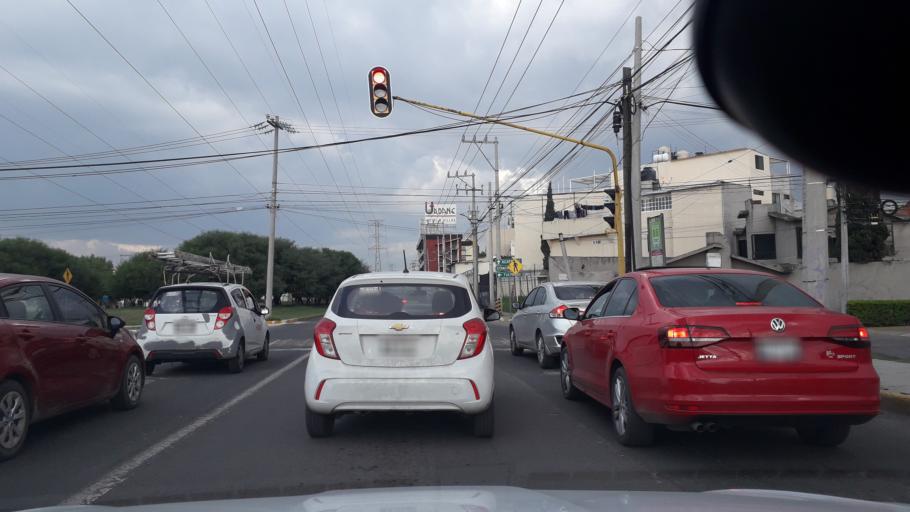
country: MX
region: Mexico
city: Santiago Teyahualco
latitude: 19.6416
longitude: -99.1167
